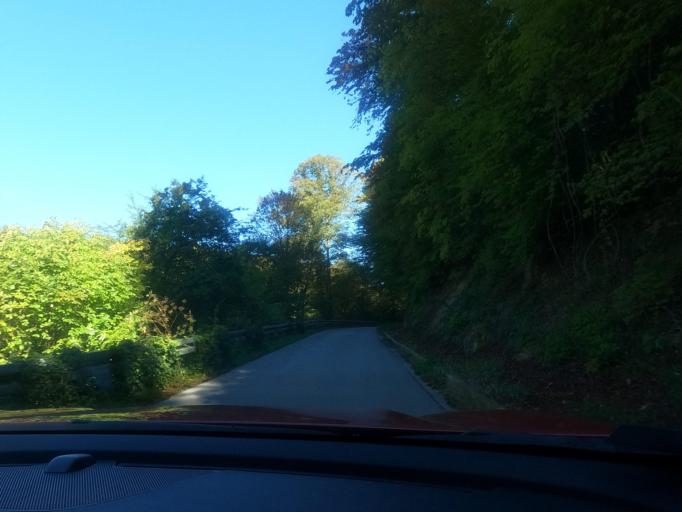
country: HR
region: Sisacko-Moslavacka
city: Petrinja
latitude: 45.3988
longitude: 16.2445
